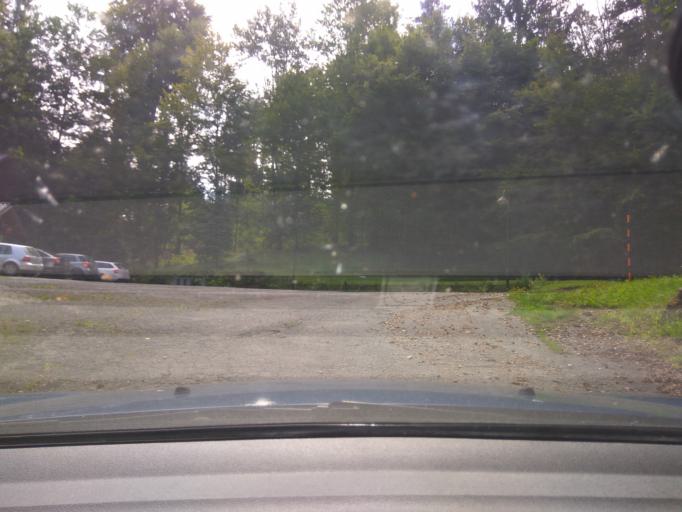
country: SK
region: Banskobystricky
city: Ziar nad Hronom
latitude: 48.5408
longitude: 18.8475
